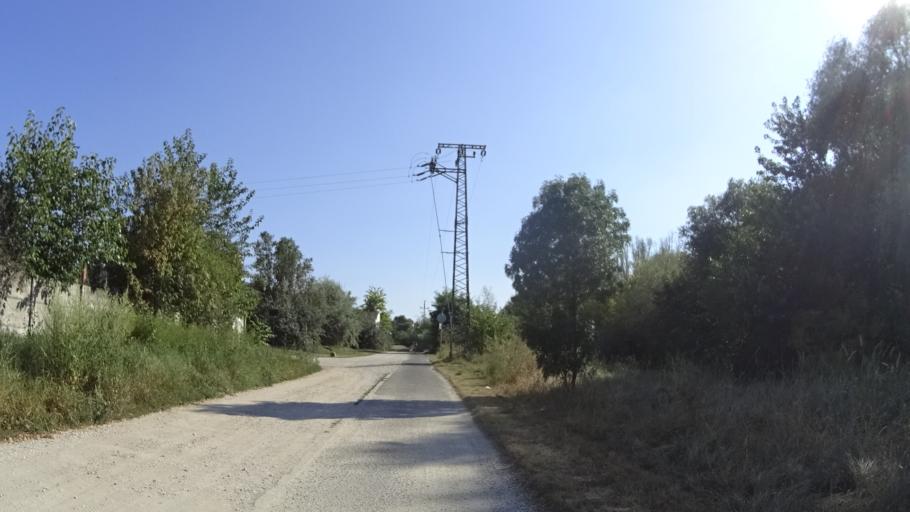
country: HU
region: Komarom-Esztergom
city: Esztergom
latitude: 47.8053
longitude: 18.7352
